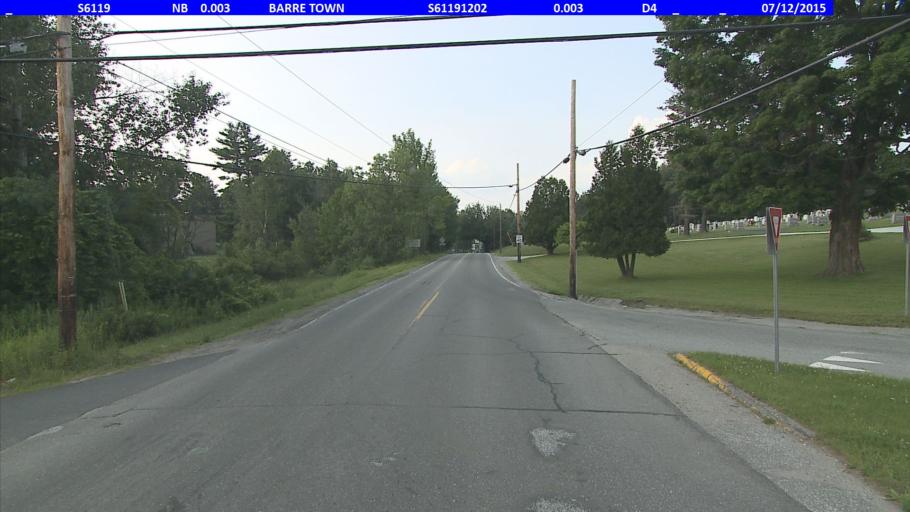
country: US
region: Vermont
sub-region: Washington County
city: South Barre
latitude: 44.1703
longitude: -72.4916
